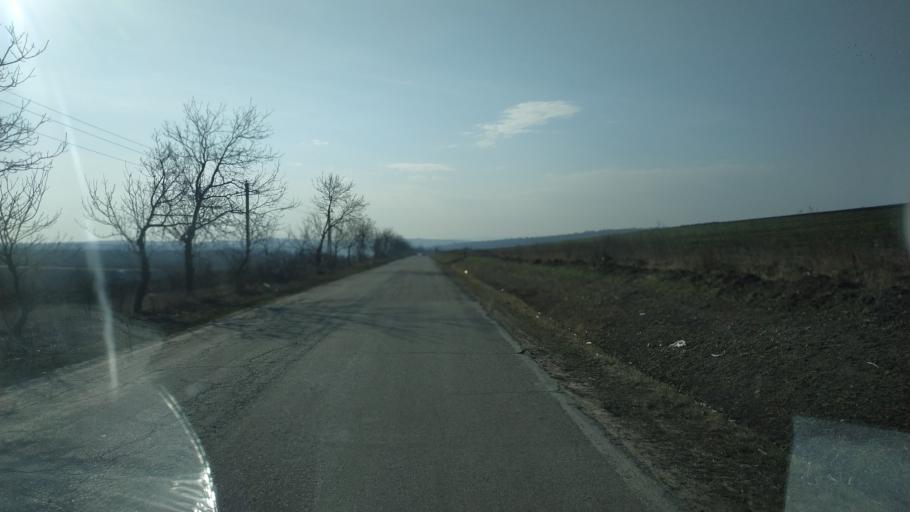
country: MD
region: Chisinau
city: Singera
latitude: 46.8520
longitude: 29.0225
